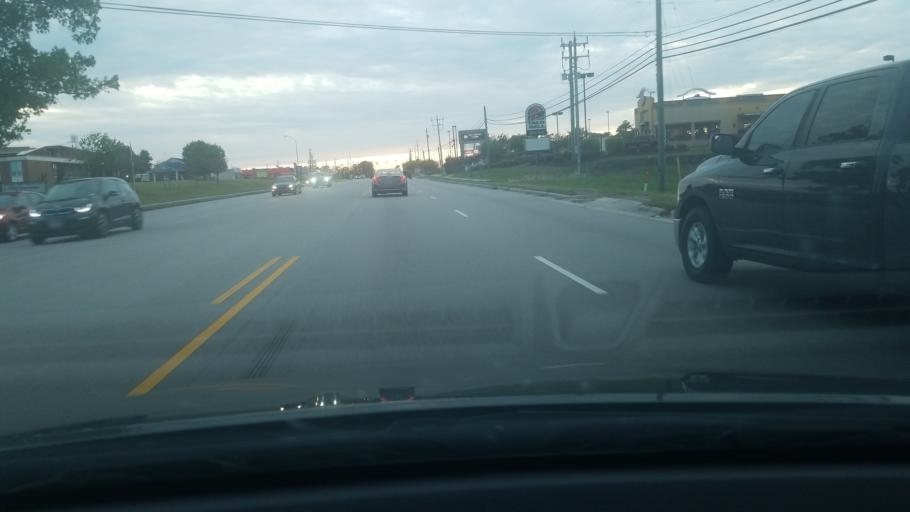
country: US
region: North Carolina
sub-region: Onslow County
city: Swansboro
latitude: 34.6918
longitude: -77.1271
